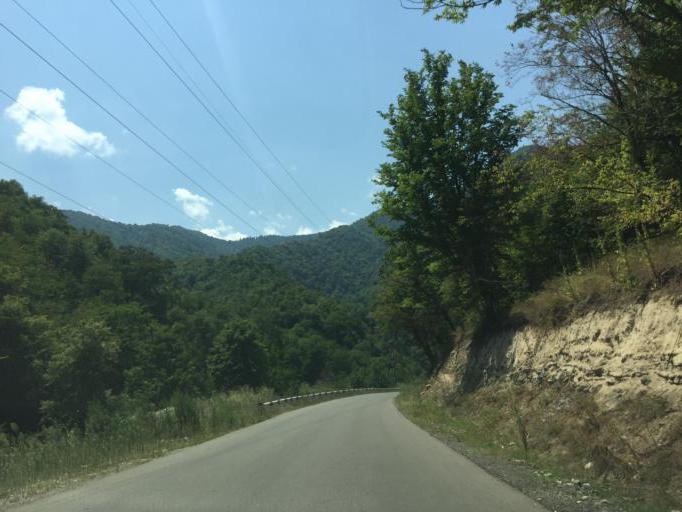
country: AZ
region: Kalbacar Rayonu
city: Kerbakhiar
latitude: 40.1277
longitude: 46.4096
